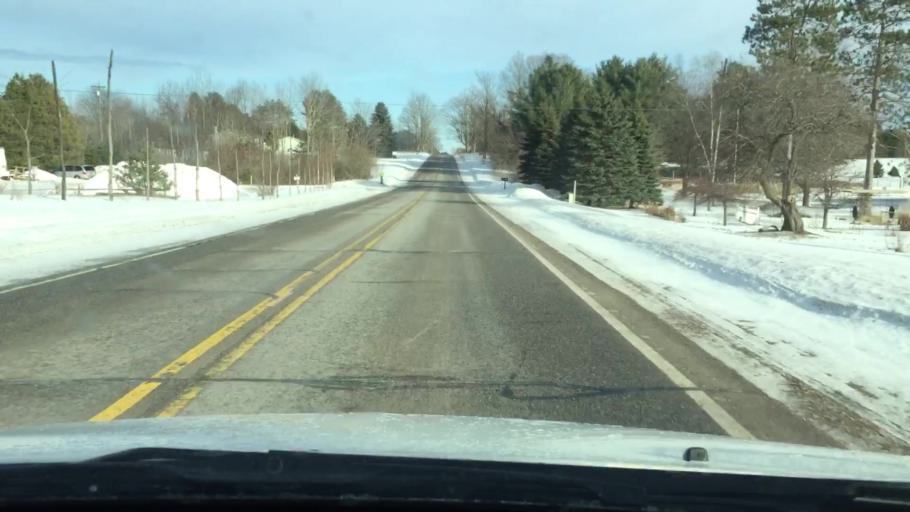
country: US
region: Michigan
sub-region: Kalkaska County
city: Kalkaska
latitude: 44.6405
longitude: -85.1924
